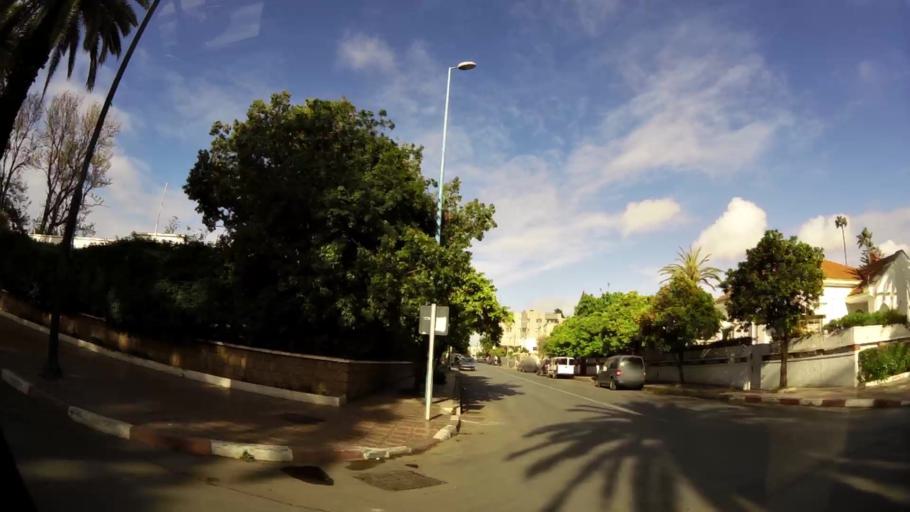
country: MA
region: Grand Casablanca
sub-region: Mohammedia
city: Mohammedia
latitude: 33.7007
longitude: -7.3935
